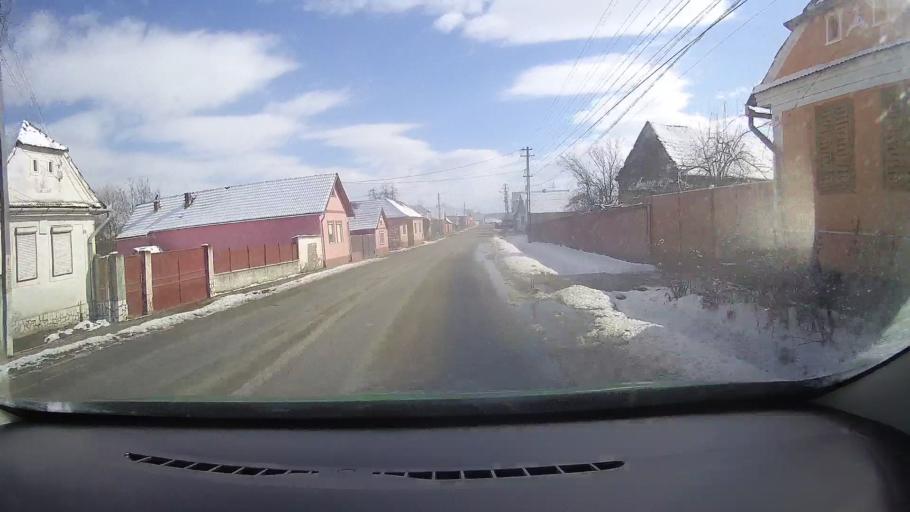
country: RO
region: Sibiu
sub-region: Comuna Barghis
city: Barghis
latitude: 45.9809
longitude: 24.5390
